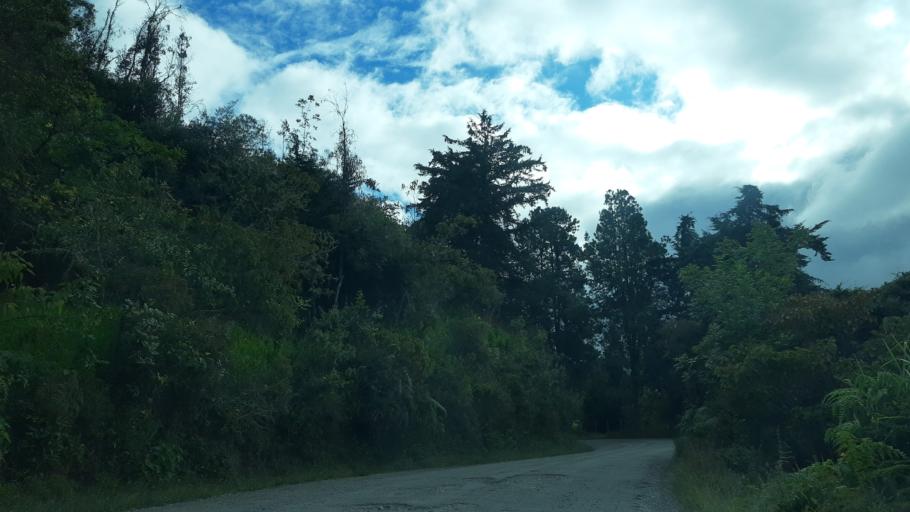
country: CO
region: Cundinamarca
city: Tenza
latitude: 5.0428
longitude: -73.4265
